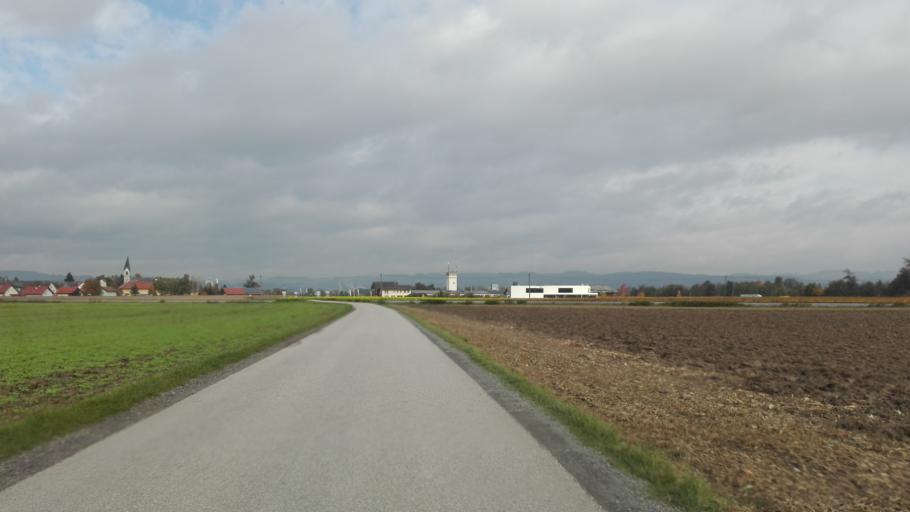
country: AT
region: Upper Austria
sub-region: Politischer Bezirk Urfahr-Umgebung
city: Feldkirchen an der Donau
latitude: 48.3313
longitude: 14.0006
